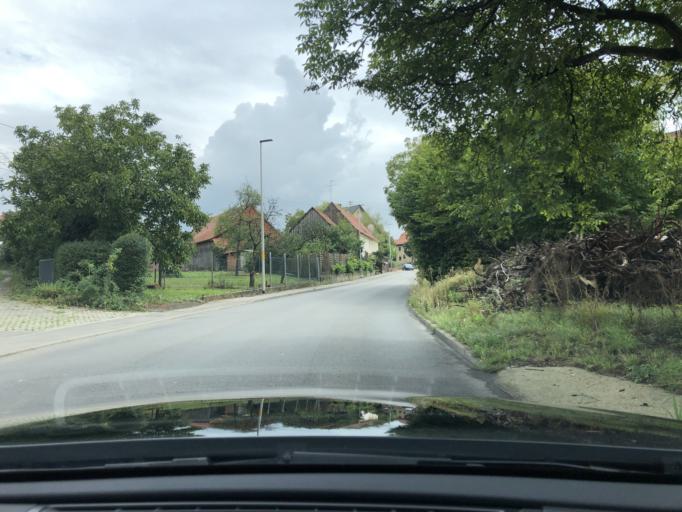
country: DE
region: Baden-Wuerttemberg
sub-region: Regierungsbezirk Stuttgart
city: Affalterbach
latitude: 48.9237
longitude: 9.3189
